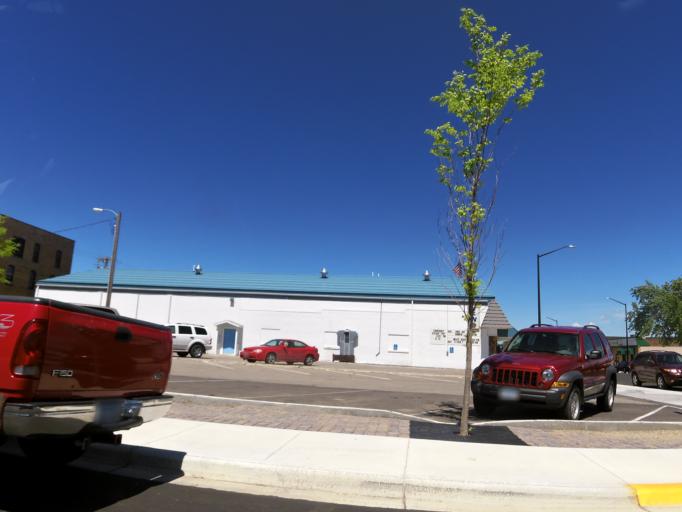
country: US
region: Minnesota
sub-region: Wadena County
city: Wadena
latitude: 46.4389
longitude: -95.1371
